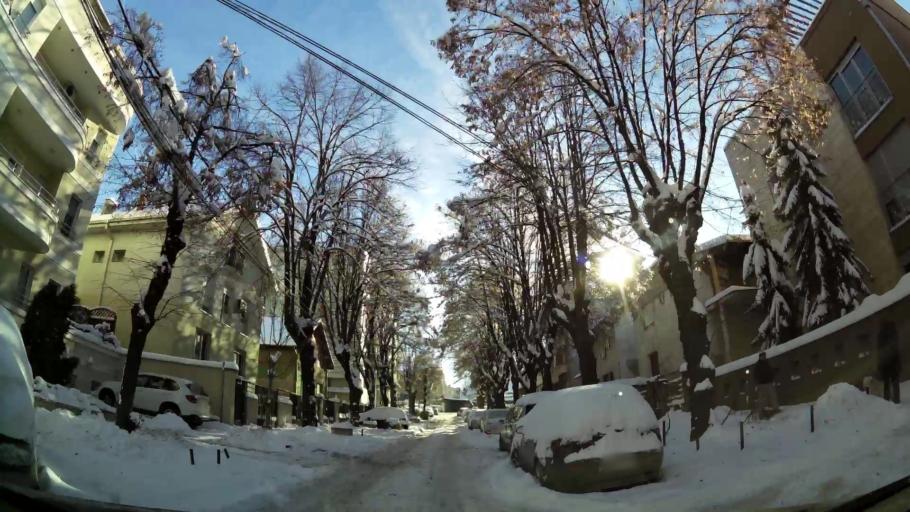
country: RS
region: Central Serbia
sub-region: Belgrade
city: Palilula
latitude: 44.7929
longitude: 20.5014
